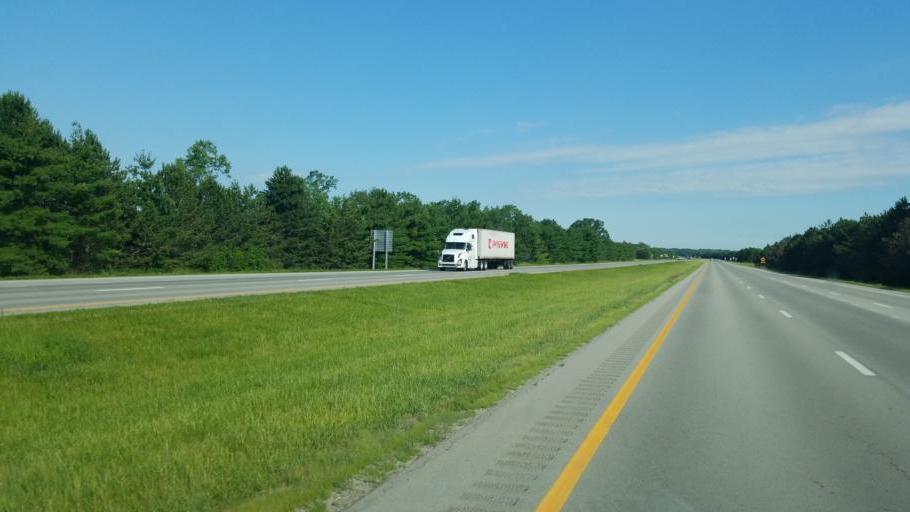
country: US
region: Ohio
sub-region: Wyandot County
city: Carey
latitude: 40.9727
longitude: -83.4875
